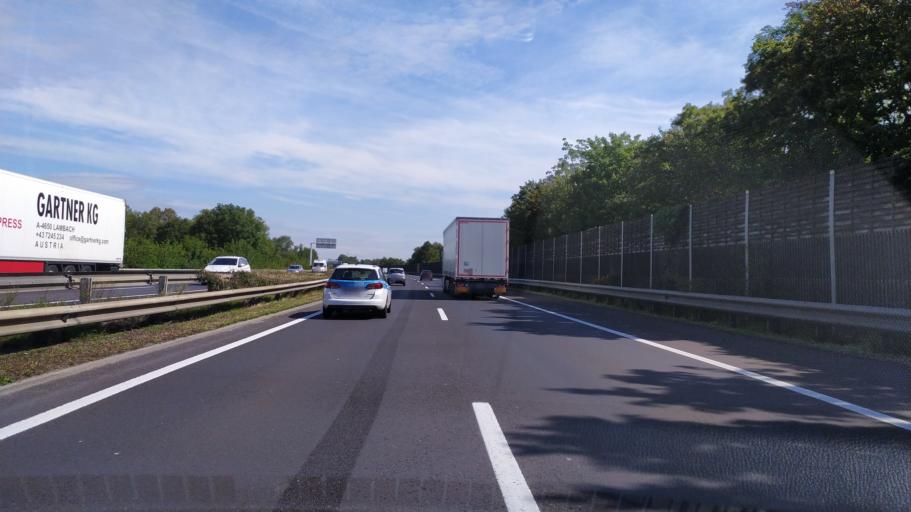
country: AT
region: Upper Austria
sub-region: Wels-Land
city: Marchtrenk
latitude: 48.1765
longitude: 14.1325
